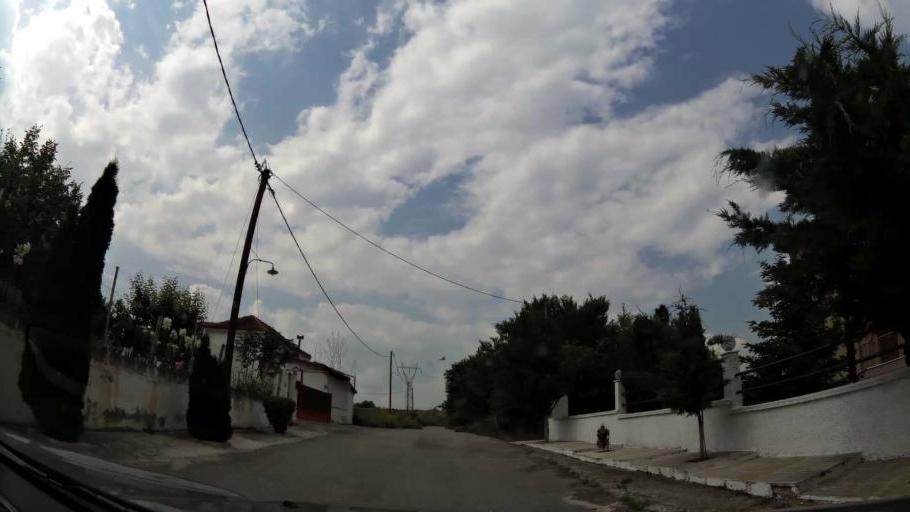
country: GR
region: West Macedonia
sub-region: Nomos Kozanis
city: Koila
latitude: 40.3478
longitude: 21.8221
